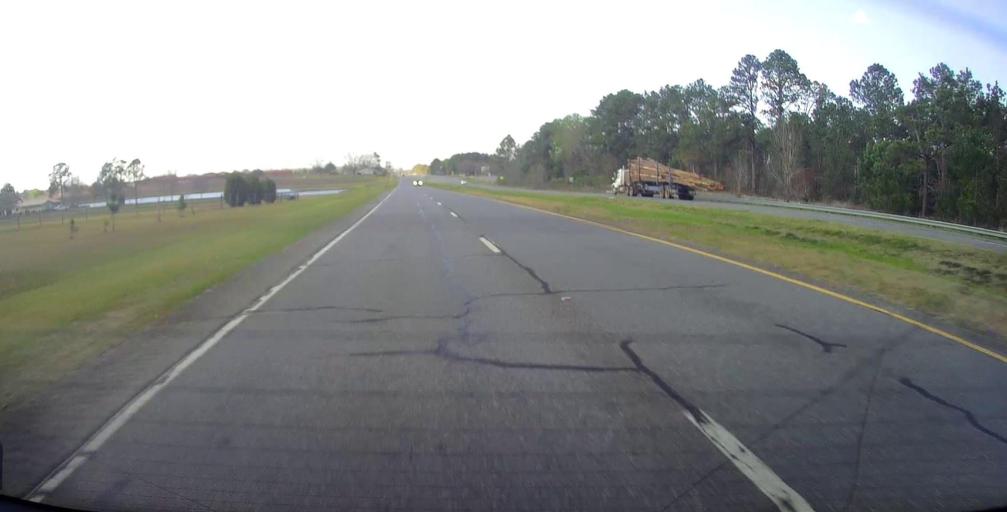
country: US
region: Georgia
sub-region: Dodge County
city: Eastman
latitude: 32.1664
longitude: -83.1539
